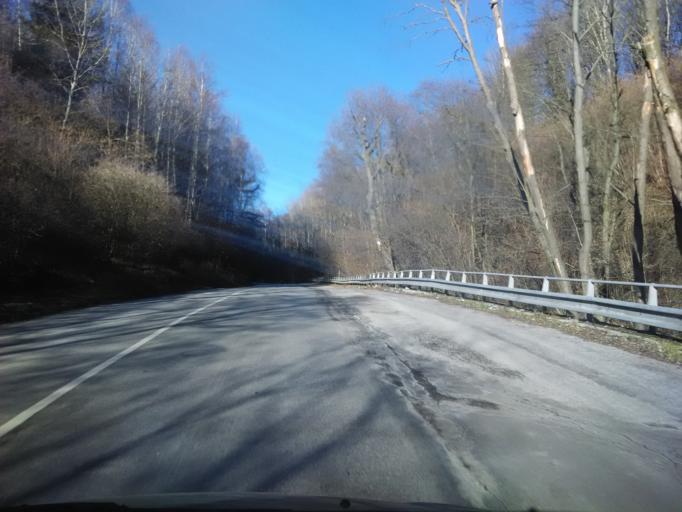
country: SK
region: Banskobystricky
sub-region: Okres Ziar nad Hronom
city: Kremnica
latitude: 48.7224
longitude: 18.9168
